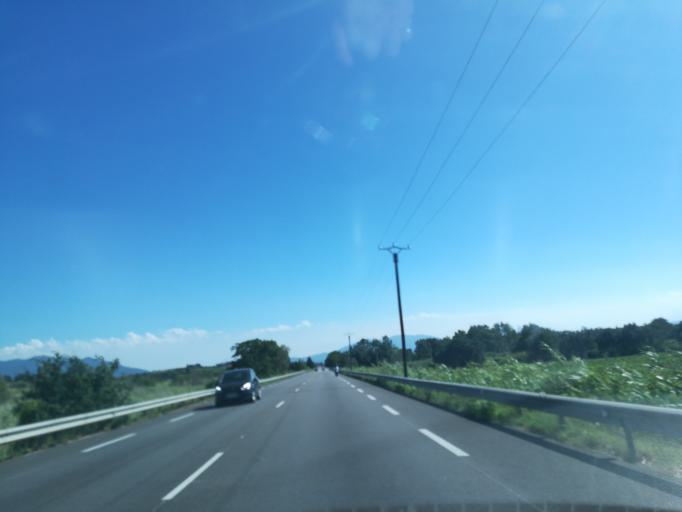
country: FR
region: Languedoc-Roussillon
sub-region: Departement des Pyrenees-Orientales
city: Pollestres
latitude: 42.6198
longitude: 2.8660
